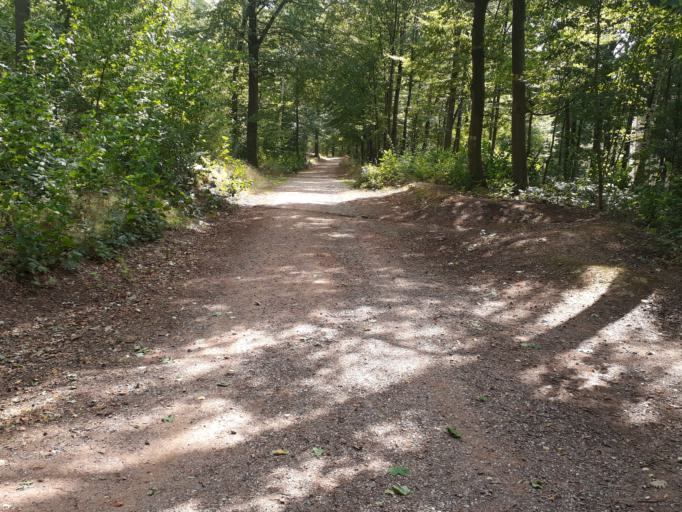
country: DE
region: Rheinland-Pfalz
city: Kaiserslautern
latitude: 49.4307
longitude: 7.7866
